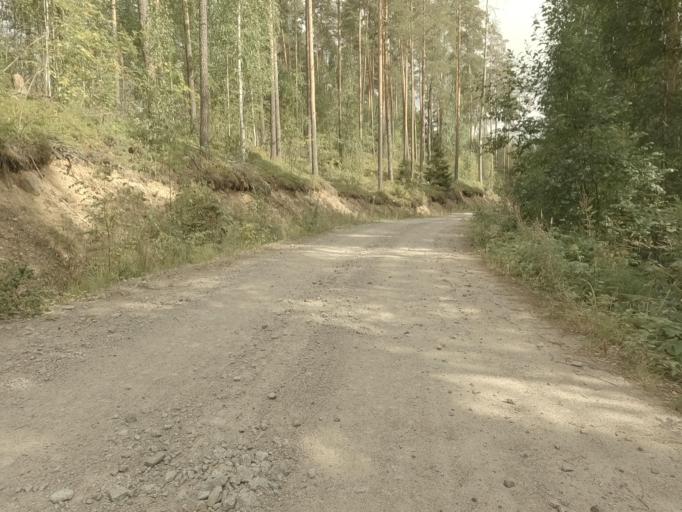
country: RU
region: Leningrad
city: Kamennogorsk
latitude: 60.9750
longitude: 29.1760
